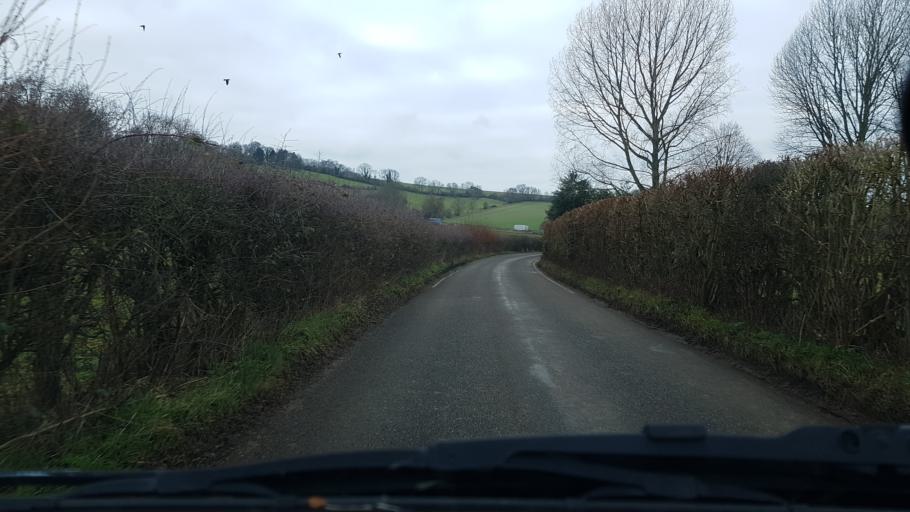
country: GB
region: England
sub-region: Hampshire
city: Andover
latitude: 51.2833
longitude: -1.4686
